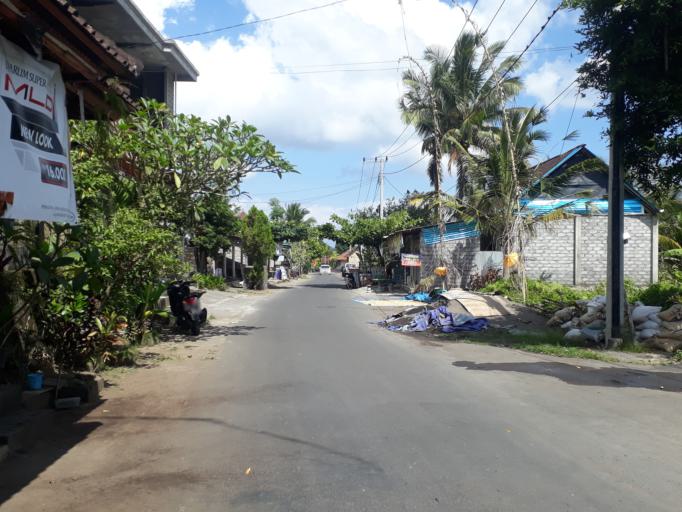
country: ID
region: Bali
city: Banjar Wangsian
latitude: -8.4717
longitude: 115.4443
